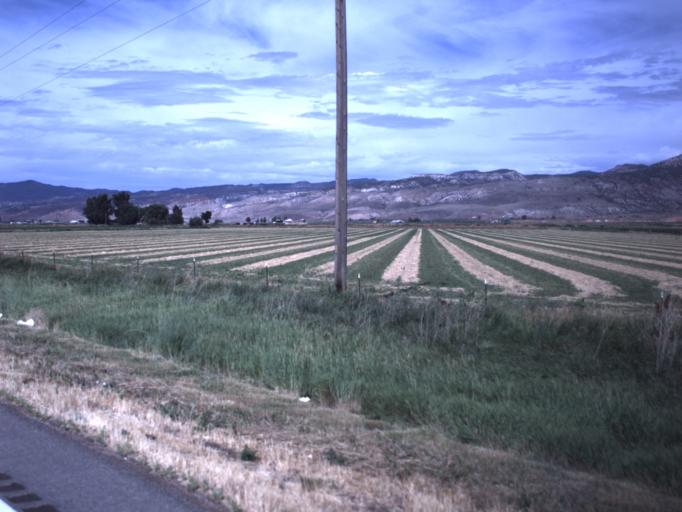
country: US
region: Utah
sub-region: Sevier County
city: Richfield
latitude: 38.8037
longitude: -112.0260
